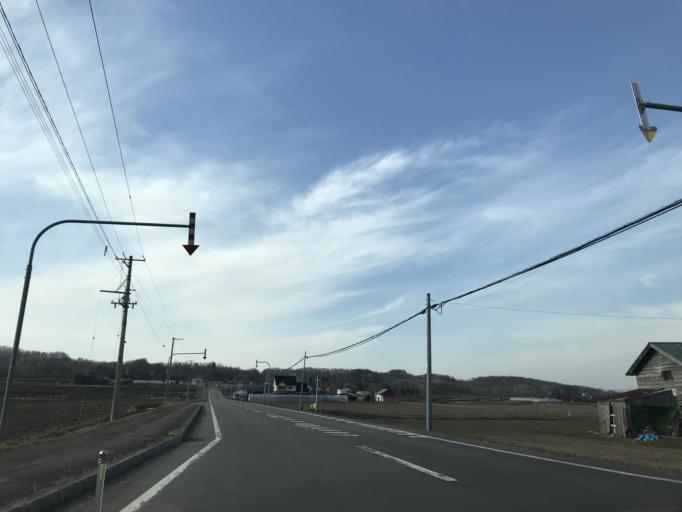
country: JP
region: Hokkaido
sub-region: Asahikawa-shi
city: Asahikawa
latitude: 43.7010
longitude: 142.3468
